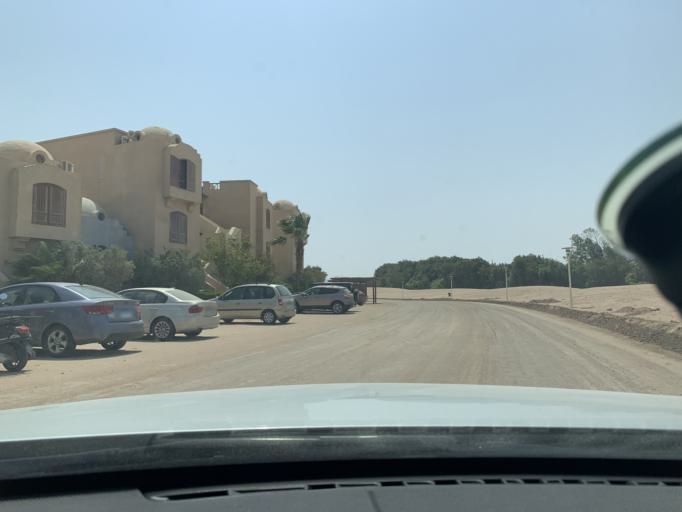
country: EG
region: Red Sea
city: El Gouna
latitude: 27.3892
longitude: 33.6676
